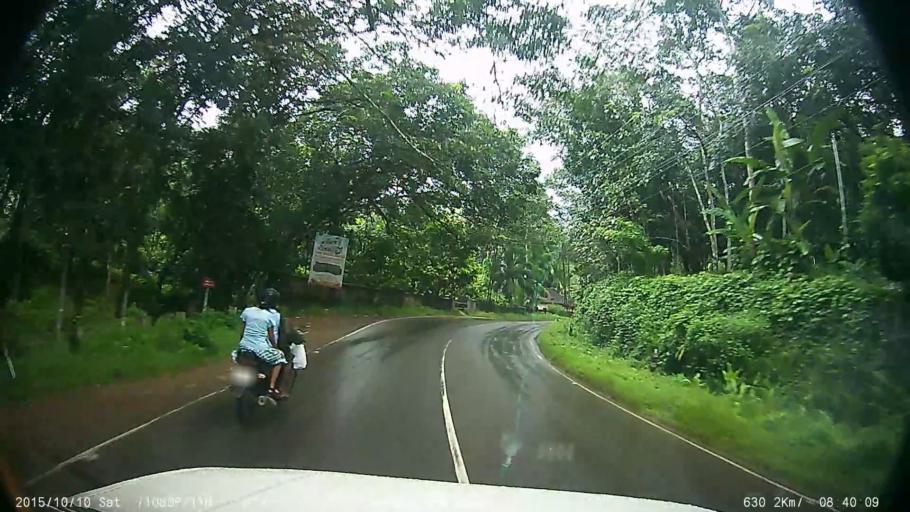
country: IN
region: Kerala
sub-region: Kottayam
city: Palackattumala
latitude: 9.7573
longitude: 76.5526
